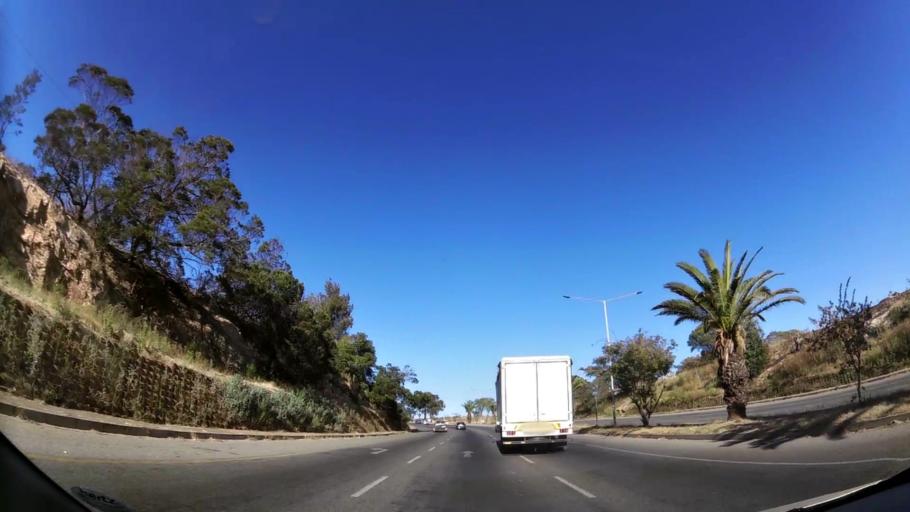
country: ZA
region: Gauteng
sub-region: West Rand District Municipality
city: Krugersdorp
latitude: -26.1109
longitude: 27.7769
